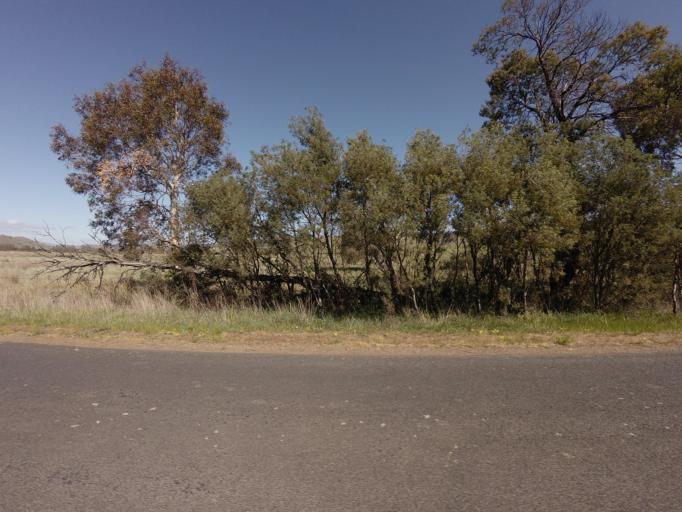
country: AU
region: Tasmania
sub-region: Derwent Valley
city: New Norfolk
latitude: -42.5367
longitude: 146.7274
